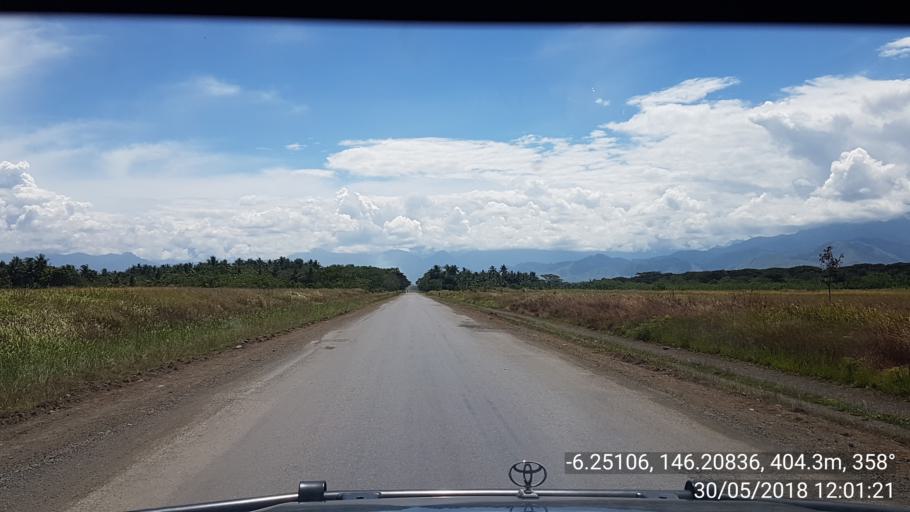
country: PG
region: Eastern Highlands
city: Kainantu
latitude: -6.2511
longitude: 146.2084
